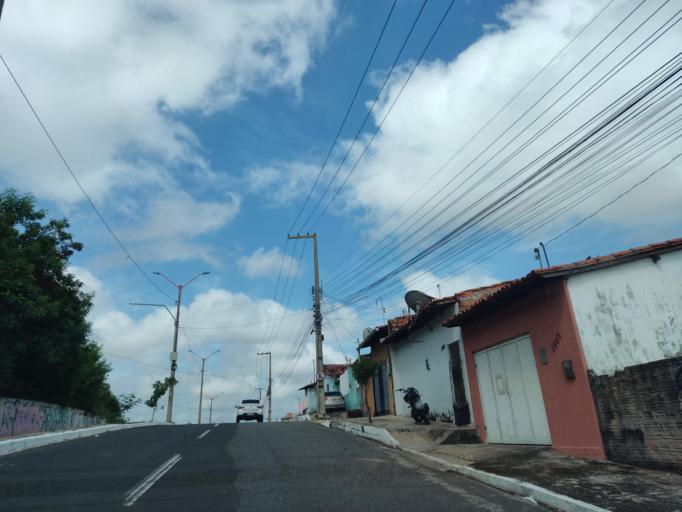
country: BR
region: Piaui
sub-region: Teresina
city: Teresina
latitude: -5.0718
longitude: -42.8071
